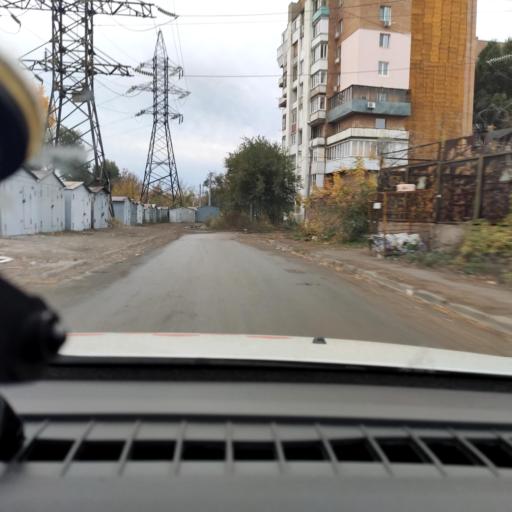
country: RU
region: Samara
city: Samara
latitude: 53.1914
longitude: 50.2215
